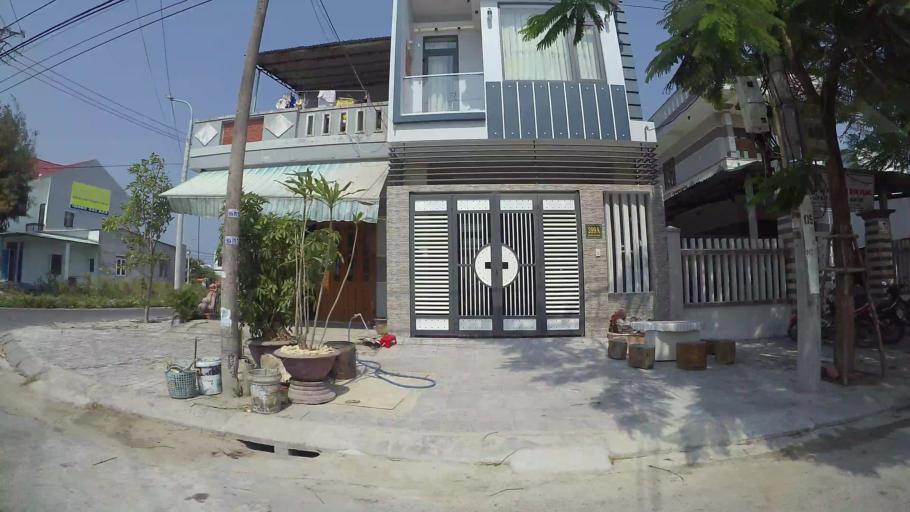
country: VN
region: Da Nang
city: Ngu Hanh Son
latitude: 15.9898
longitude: 108.2674
